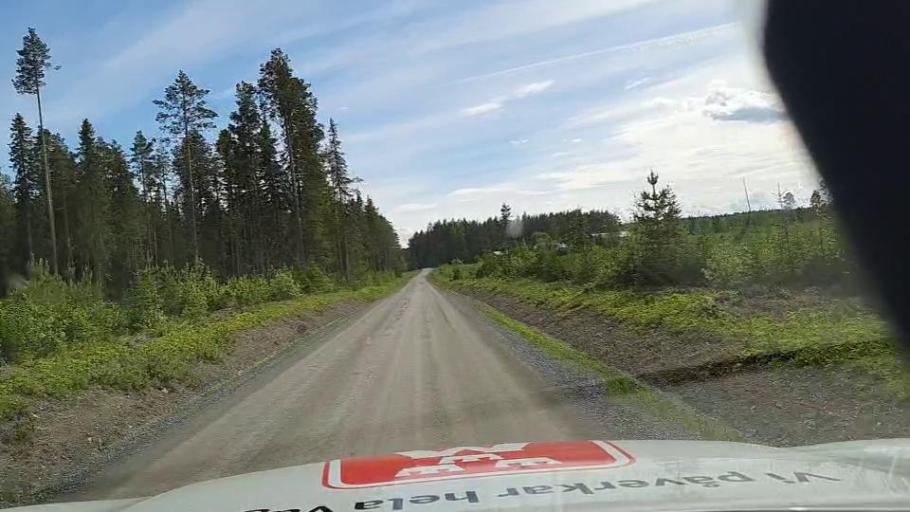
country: SE
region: Jaemtland
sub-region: OEstersunds Kommun
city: Brunflo
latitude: 62.9965
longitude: 14.8069
